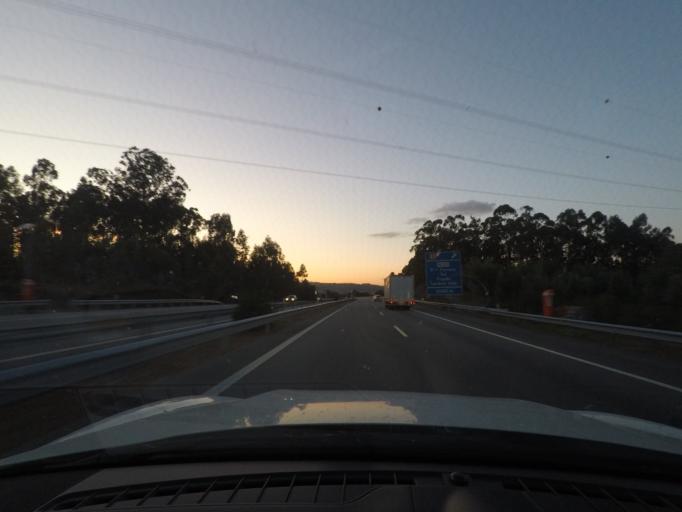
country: PT
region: Porto
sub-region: Pacos de Ferreira
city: Pacos de Ferreira
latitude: 41.2617
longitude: -8.3741
